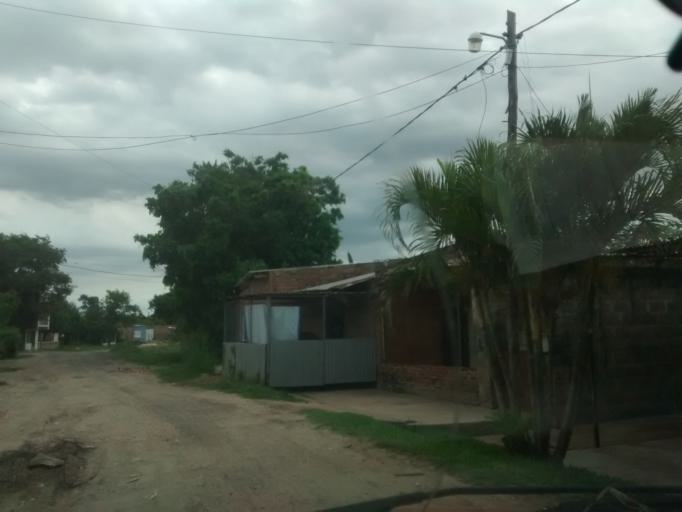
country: AR
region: Chaco
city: Resistencia
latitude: -27.4295
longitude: -58.9772
